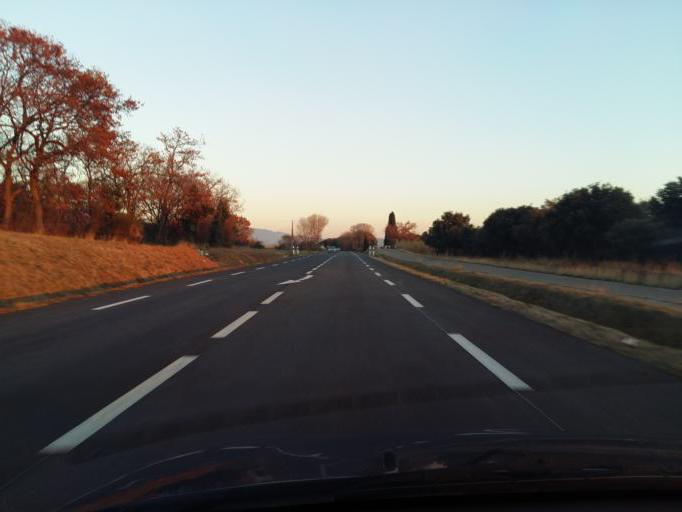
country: FR
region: Provence-Alpes-Cote d'Azur
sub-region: Departement du Vaucluse
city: Grillon
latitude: 44.3919
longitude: 4.9499
